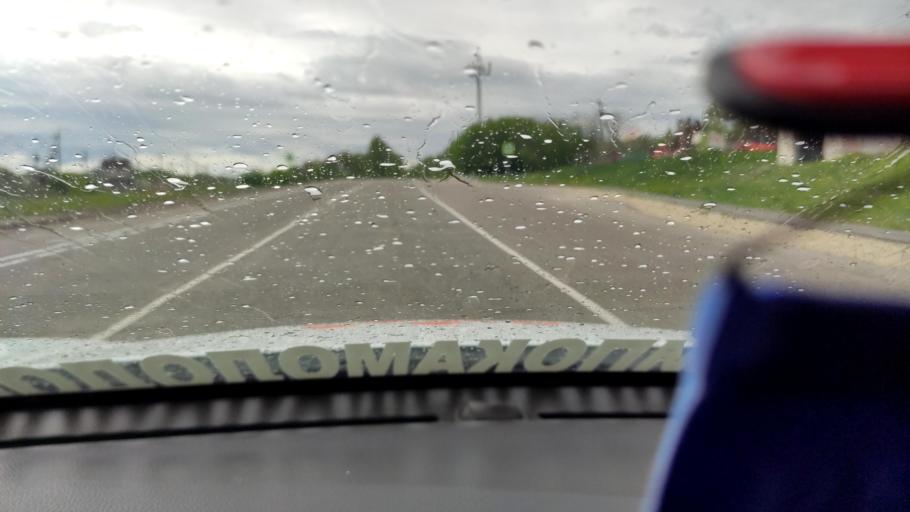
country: RU
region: Voronezj
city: Imeni Pervogo Maya
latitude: 50.7518
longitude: 39.3881
